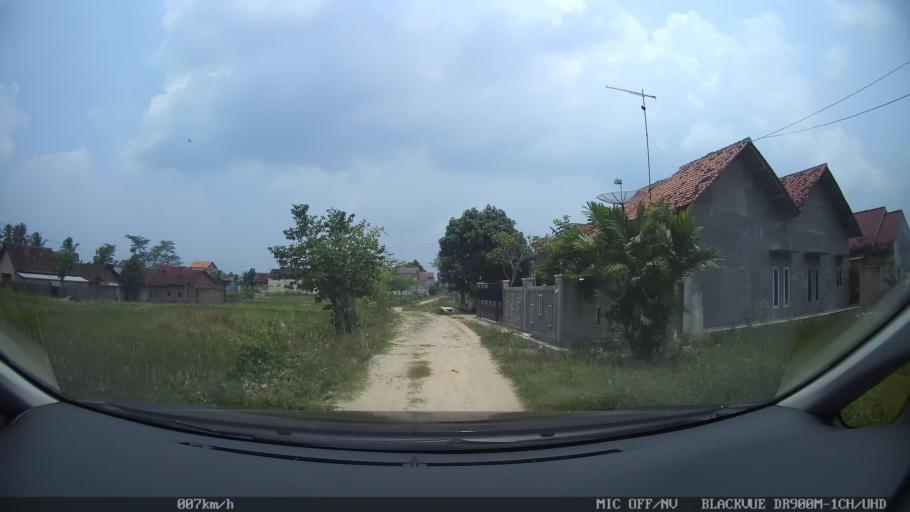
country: ID
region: Lampung
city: Pringsewu
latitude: -5.3531
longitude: 104.9623
